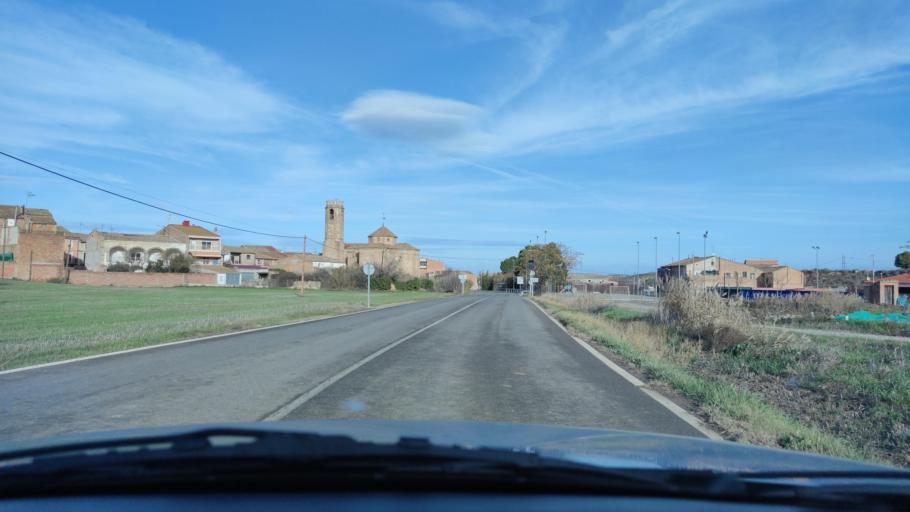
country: ES
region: Catalonia
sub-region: Provincia de Lleida
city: Alcano
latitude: 41.4795
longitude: 0.6183
